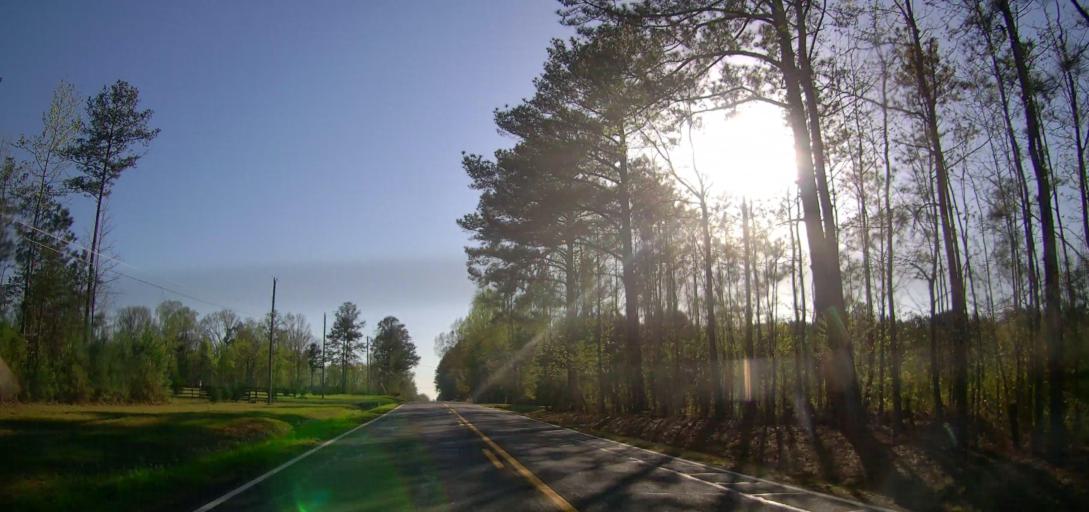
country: US
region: Georgia
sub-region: Butts County
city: Indian Springs
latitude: 33.1963
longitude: -83.9439
